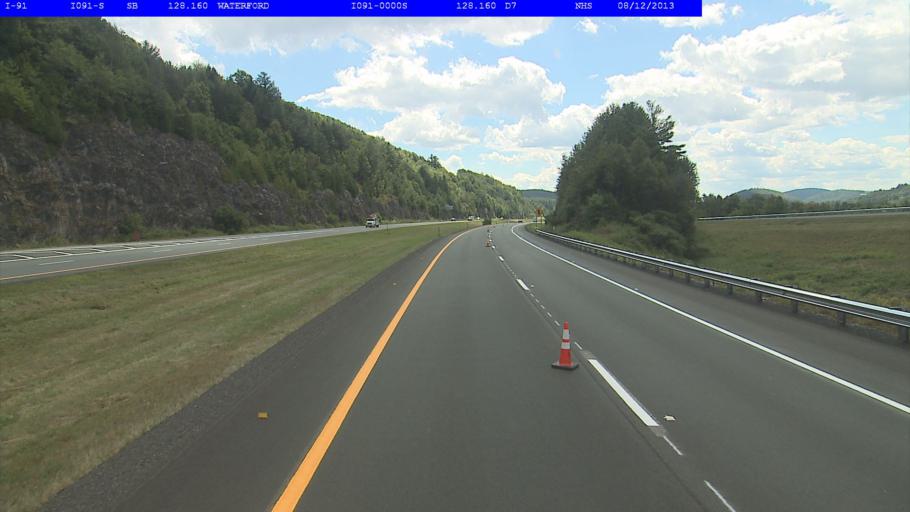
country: US
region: Vermont
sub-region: Caledonia County
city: Saint Johnsbury
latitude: 44.3952
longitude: -72.0176
